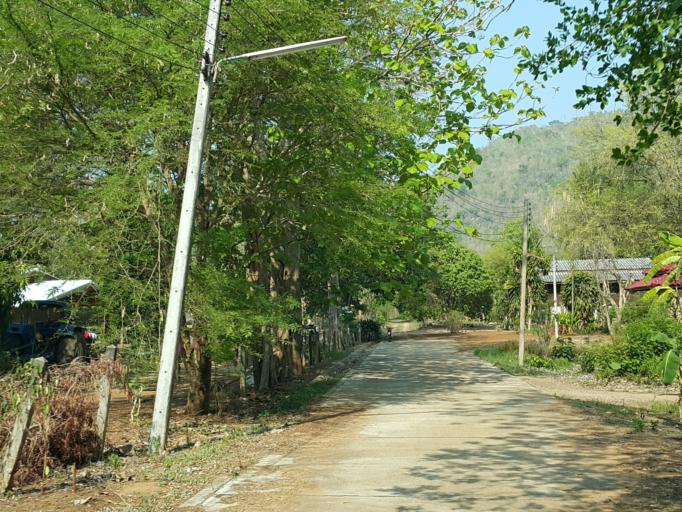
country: TH
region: Kanchanaburi
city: Sai Yok
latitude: 14.1313
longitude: 99.1282
